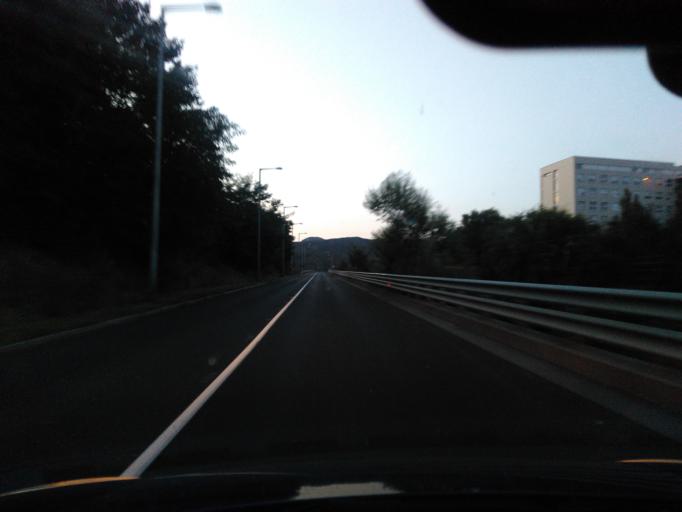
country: HU
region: Nograd
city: Salgotarjan
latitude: 48.1137
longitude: 19.8090
